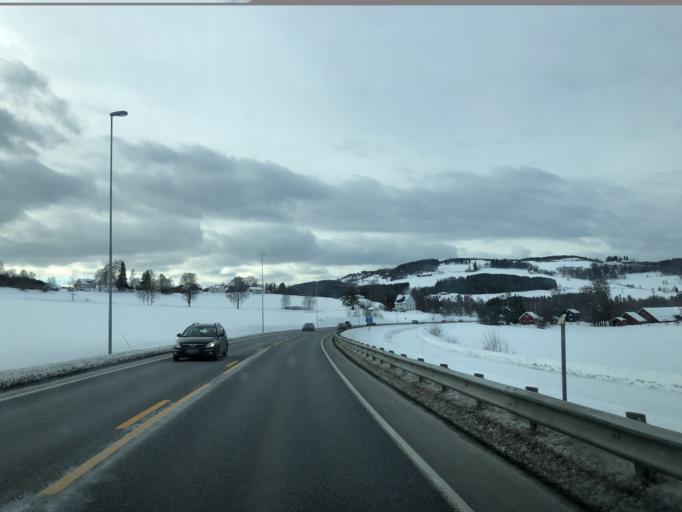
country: NO
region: Hedmark
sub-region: Ringsaker
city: Moelv
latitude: 60.8833
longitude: 10.6811
